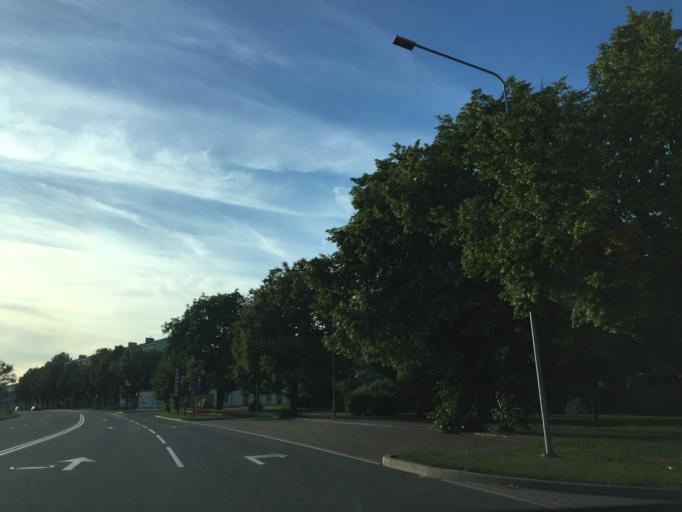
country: LV
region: Ventspils
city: Ventspils
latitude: 57.4009
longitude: 21.5845
